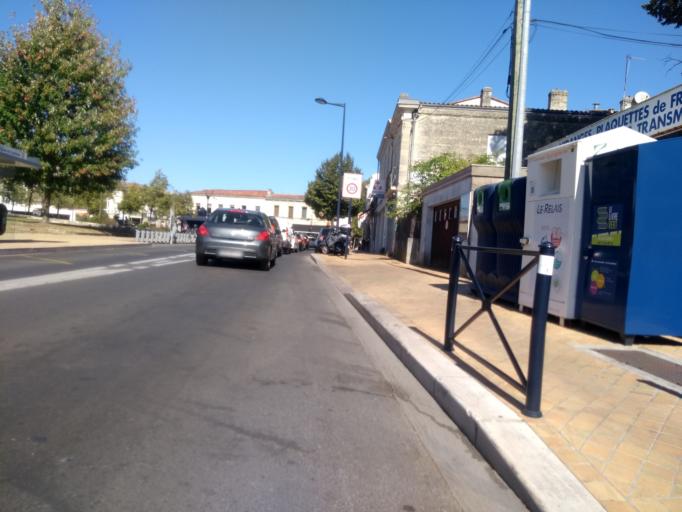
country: FR
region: Aquitaine
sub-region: Departement de la Gironde
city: Le Bouscat
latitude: 44.8514
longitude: -0.6141
